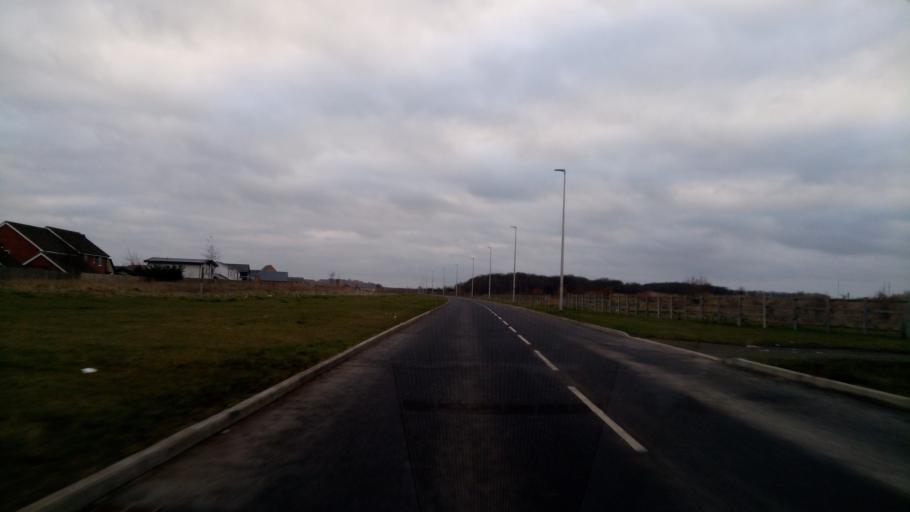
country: GB
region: England
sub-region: Cambridgeshire
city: Yaxley
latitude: 52.5339
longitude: -0.2840
